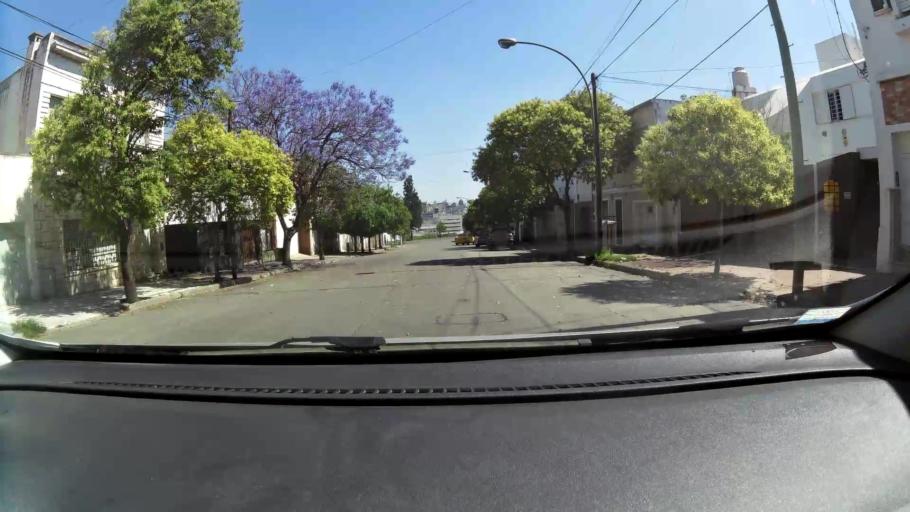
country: AR
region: Cordoba
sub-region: Departamento de Capital
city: Cordoba
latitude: -31.4032
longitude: -64.1800
